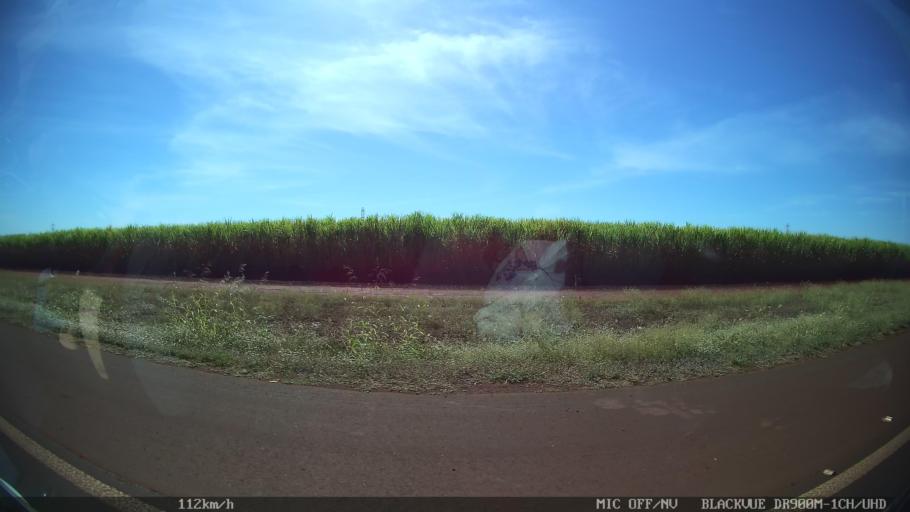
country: BR
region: Sao Paulo
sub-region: Guaira
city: Guaira
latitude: -20.4446
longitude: -48.2629
